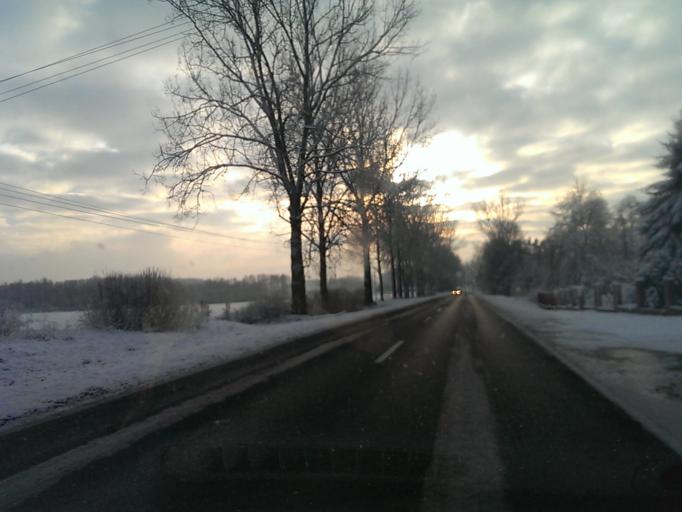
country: PL
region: Kujawsko-Pomorskie
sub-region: Powiat sepolenski
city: Wiecbork
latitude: 53.3893
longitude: 17.5132
